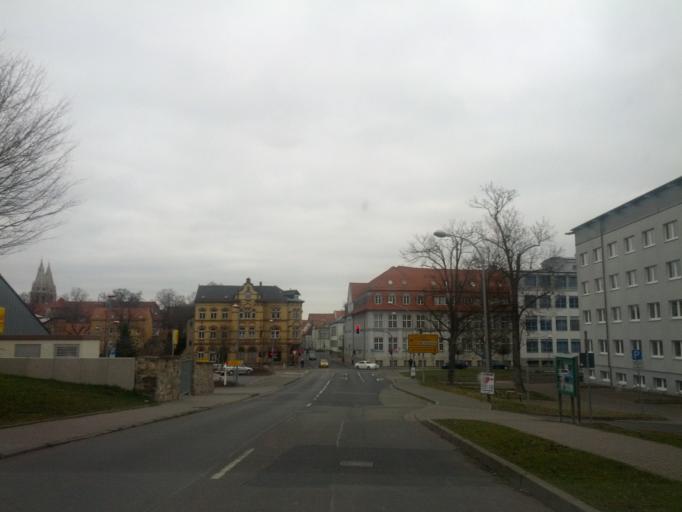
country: DE
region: Thuringia
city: Muehlhausen
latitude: 51.2040
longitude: 10.4607
